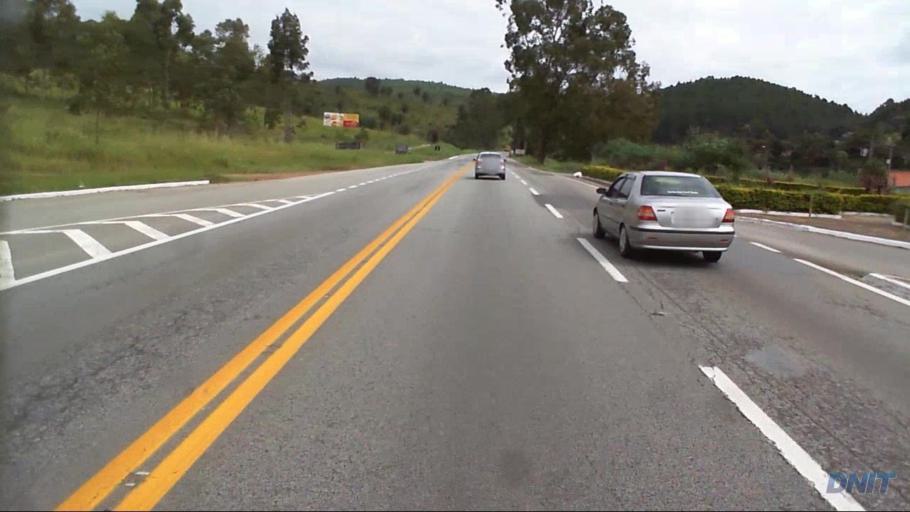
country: BR
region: Minas Gerais
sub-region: Caete
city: Caete
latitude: -19.7248
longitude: -43.5852
